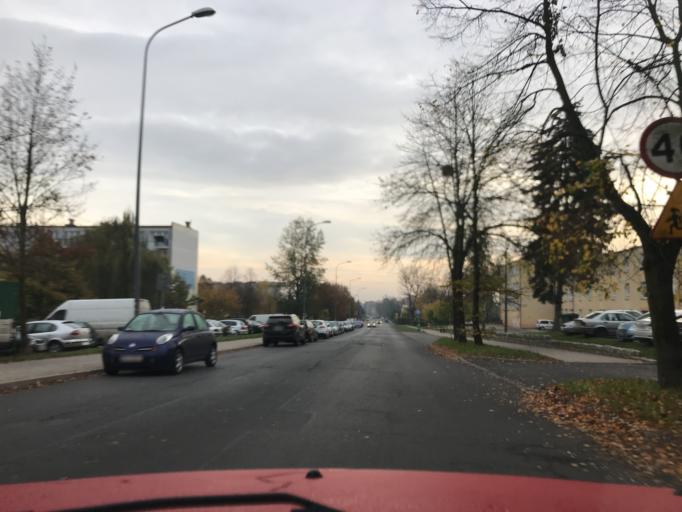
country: PL
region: Greater Poland Voivodeship
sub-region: Kalisz
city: Kalisz
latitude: 51.7532
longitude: 18.0646
